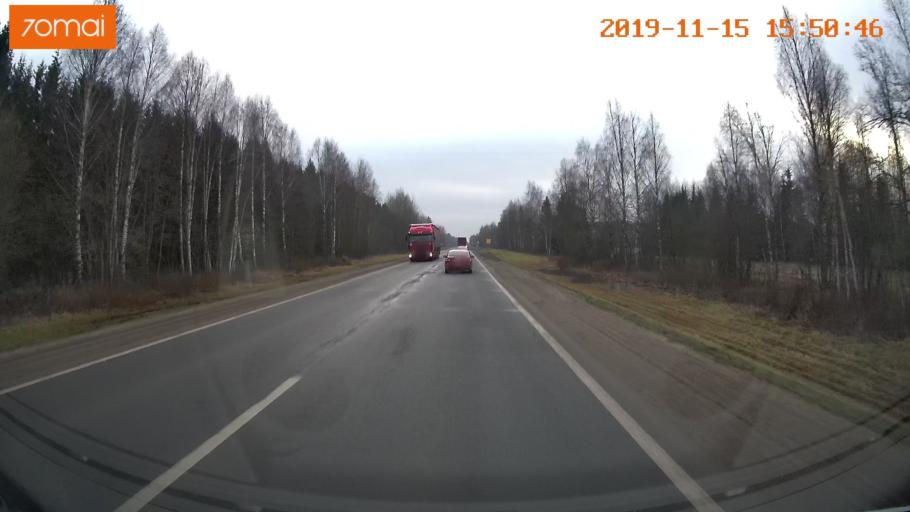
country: RU
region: Jaroslavl
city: Yaroslavl
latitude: 57.9021
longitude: 40.0123
